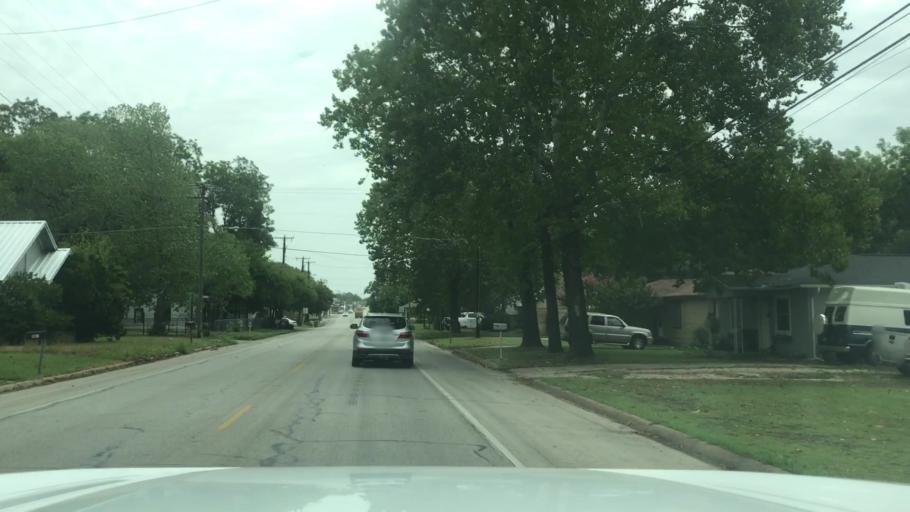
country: US
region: Texas
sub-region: Erath County
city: Dublin
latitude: 32.0861
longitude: -98.3463
